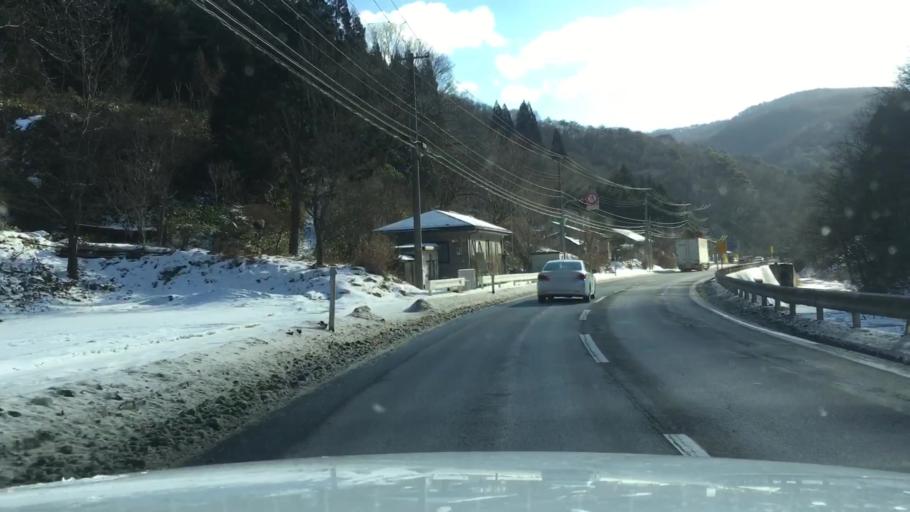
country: JP
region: Iwate
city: Tono
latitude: 39.6156
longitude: 141.4799
